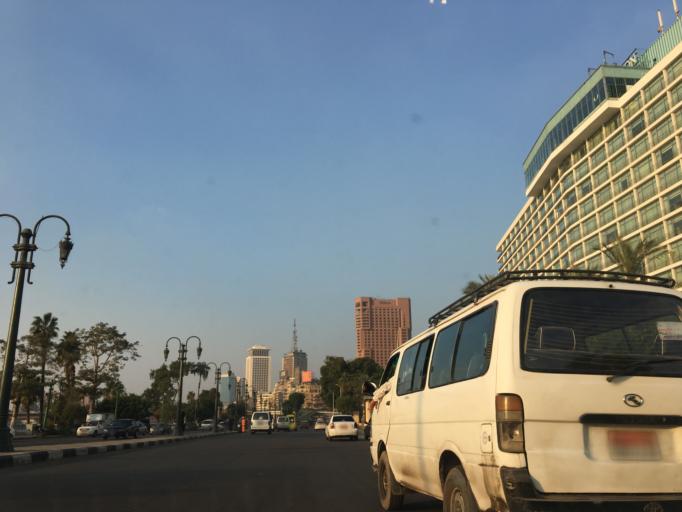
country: EG
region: Muhafazat al Qahirah
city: Cairo
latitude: 30.0451
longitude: 31.2318
